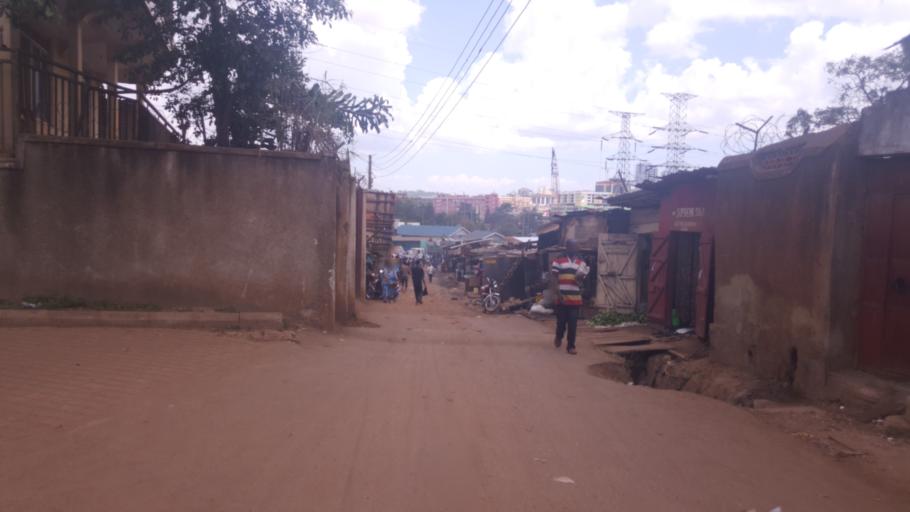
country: UG
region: Central Region
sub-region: Kampala District
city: Kampala
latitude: 0.3038
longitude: 32.5785
